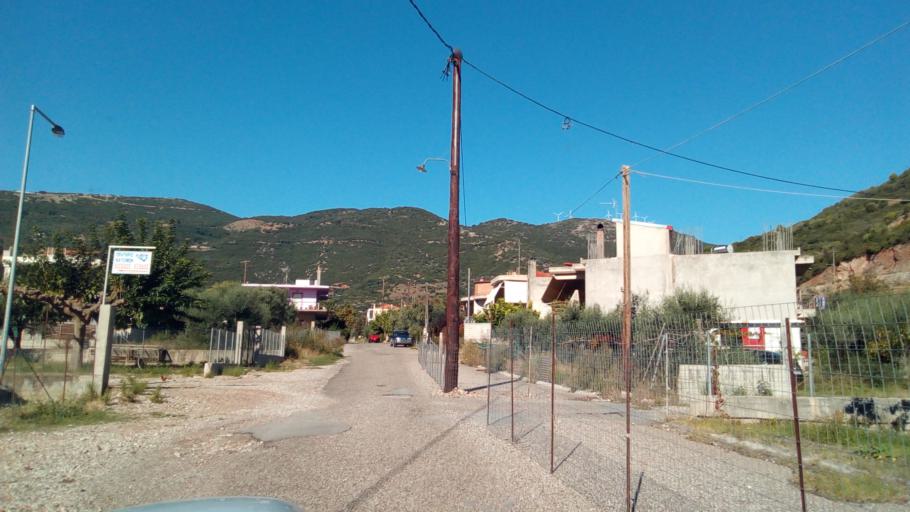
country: GR
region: West Greece
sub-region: Nomos Aitolias kai Akarnanias
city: Nafpaktos
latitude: 38.4114
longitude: 21.8478
